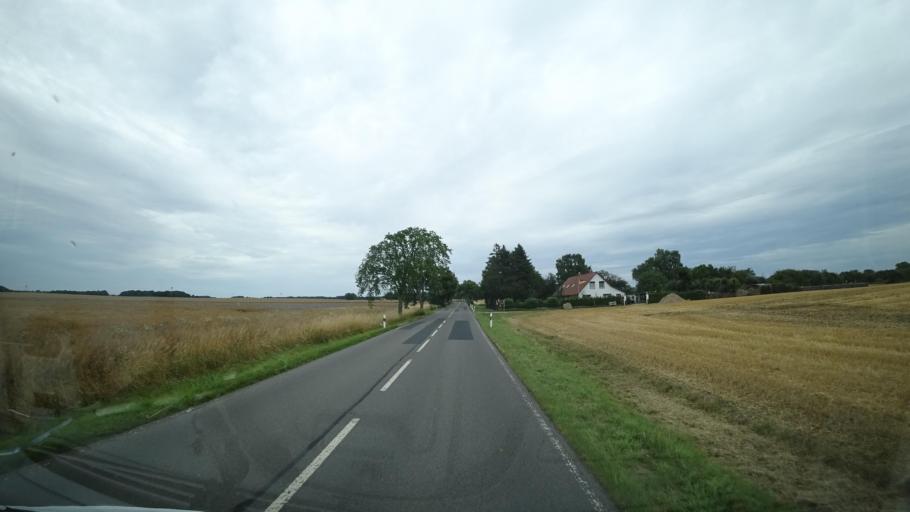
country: DE
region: Mecklenburg-Vorpommern
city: Poseritz
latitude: 54.3001
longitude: 13.3036
